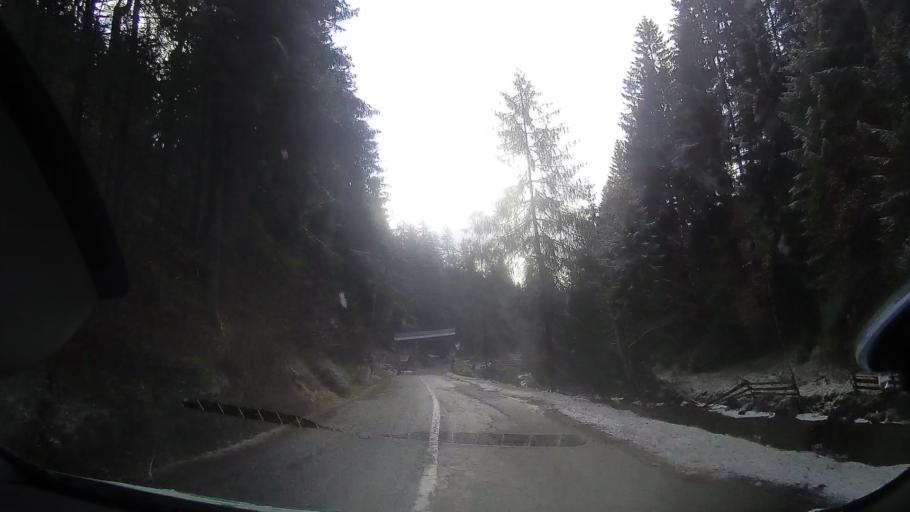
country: RO
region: Alba
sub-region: Comuna Horea
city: Horea
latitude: 46.4923
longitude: 22.9619
